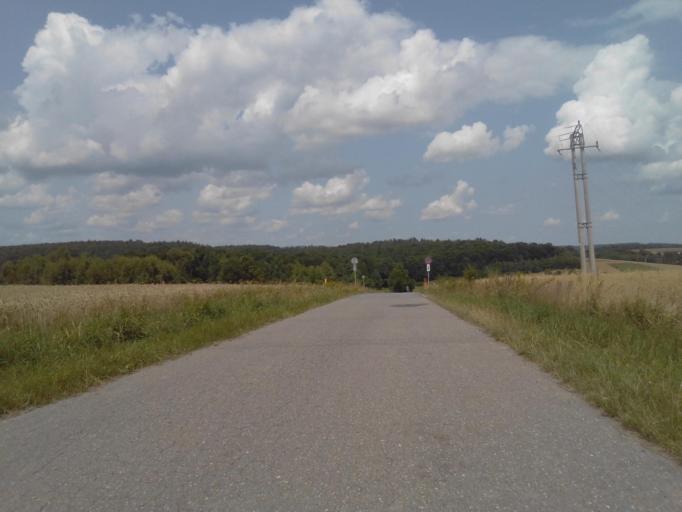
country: PL
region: Subcarpathian Voivodeship
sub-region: Powiat strzyzowski
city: Frysztak
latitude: 49.8122
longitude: 21.5823
